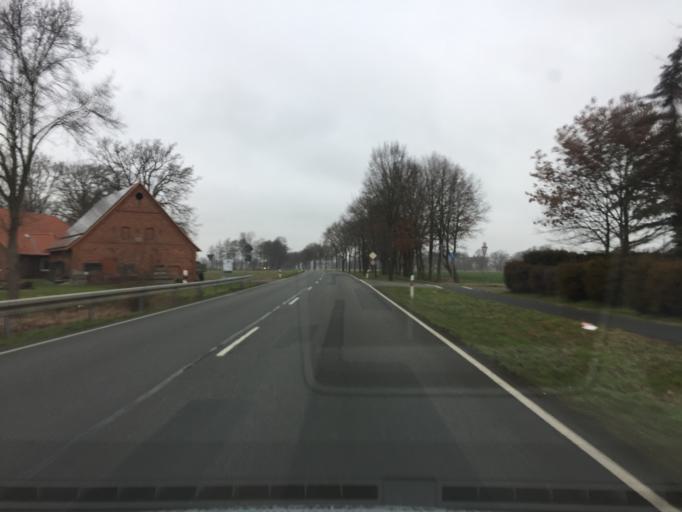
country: DE
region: Lower Saxony
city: Raddestorf
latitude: 52.4510
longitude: 8.9257
